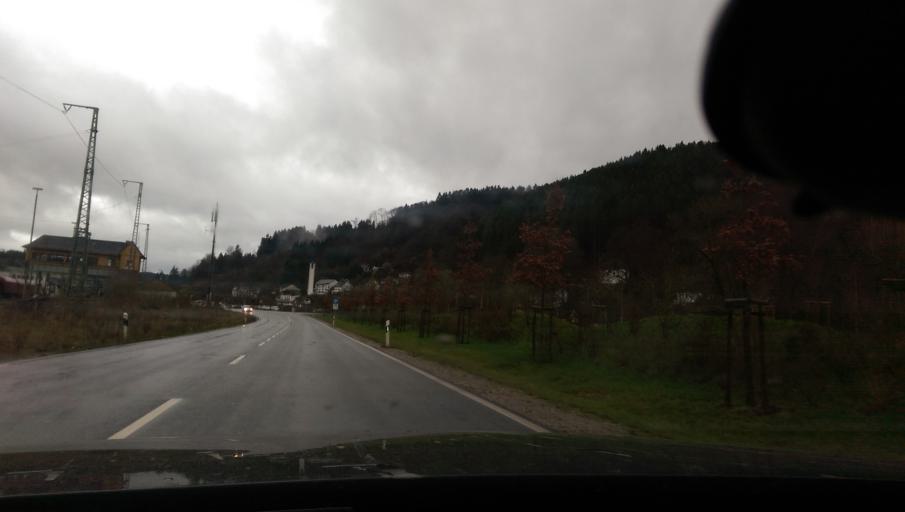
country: DE
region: North Rhine-Westphalia
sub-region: Regierungsbezirk Arnsberg
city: Finnentrop
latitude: 51.1767
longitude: 7.9653
